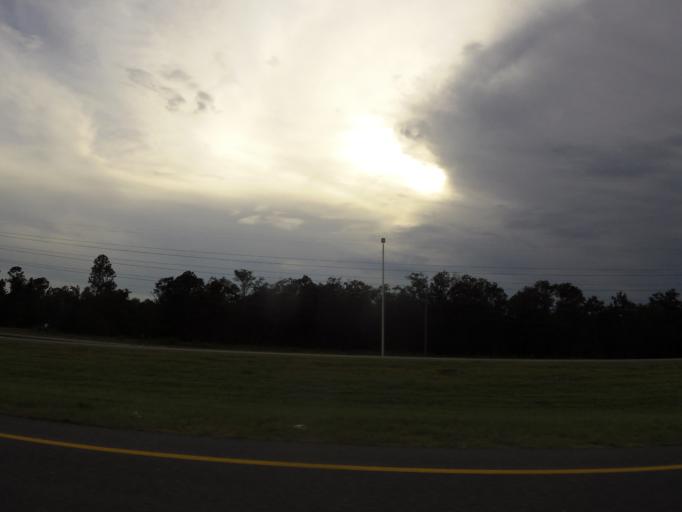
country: US
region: Florida
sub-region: Clay County
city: Lakeside
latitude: 30.1284
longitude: -81.8304
